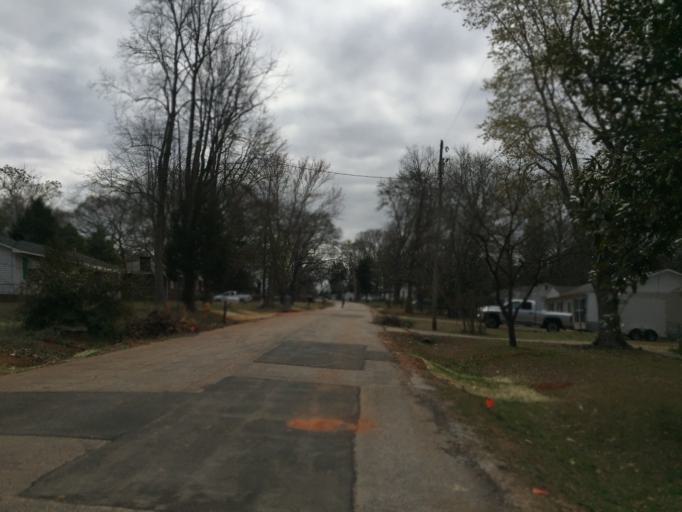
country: US
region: South Carolina
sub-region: Greenville County
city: Mauldin
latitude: 34.7823
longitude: -82.3620
